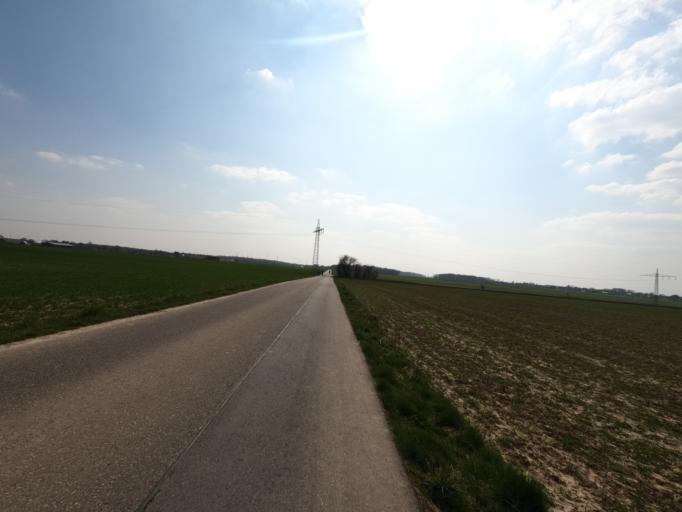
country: DE
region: North Rhine-Westphalia
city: Erkelenz
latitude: 51.0671
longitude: 6.2900
